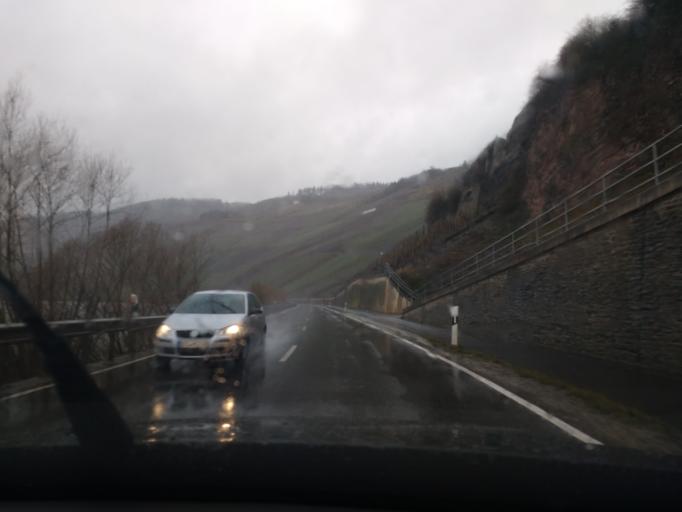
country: DE
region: Rheinland-Pfalz
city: Enkirch
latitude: 49.9825
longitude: 7.1054
